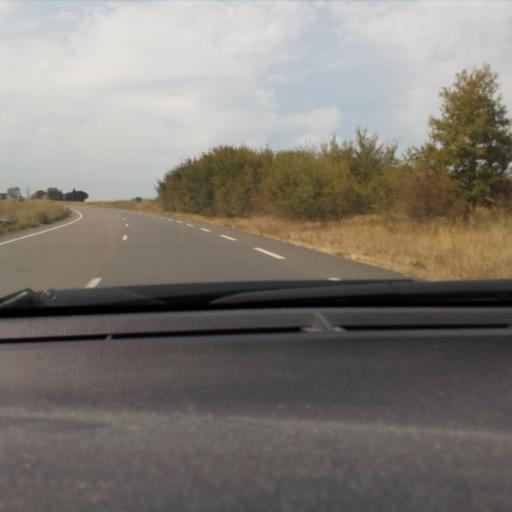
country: FR
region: Poitou-Charentes
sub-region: Departement de la Charente
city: Saint-Saturnin
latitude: 45.6708
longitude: 0.0330
